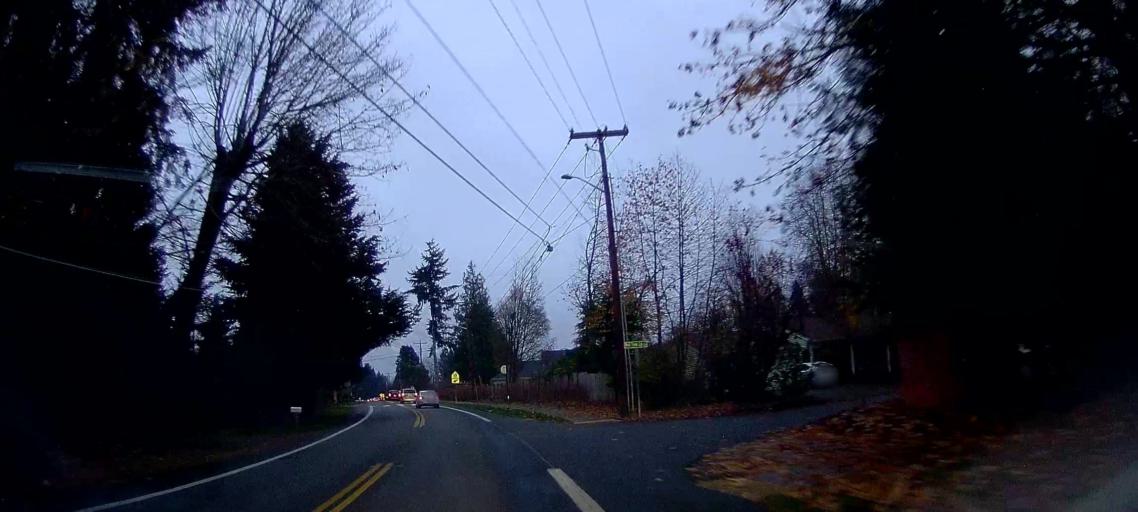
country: US
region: Washington
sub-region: Thurston County
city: Olympia
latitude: 47.0290
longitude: -122.8708
